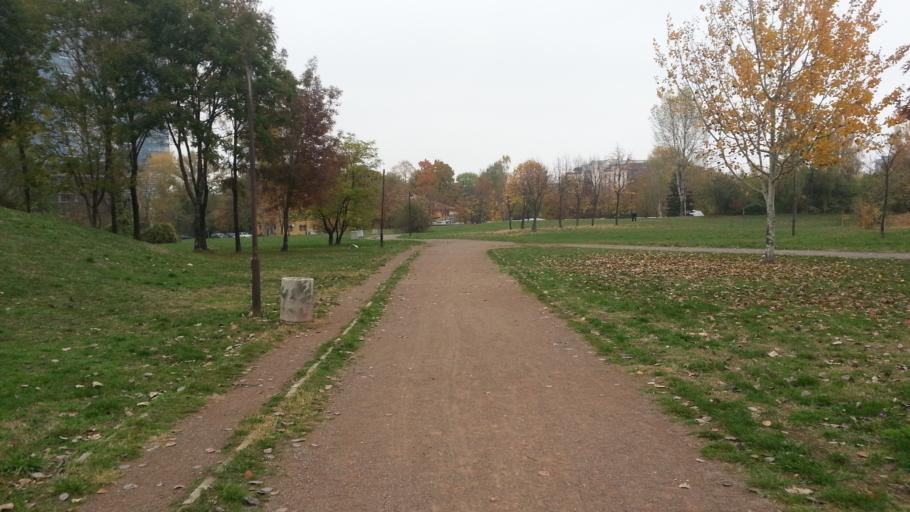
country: BG
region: Sofia-Capital
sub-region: Stolichna Obshtina
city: Sofia
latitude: 42.6795
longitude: 23.3168
